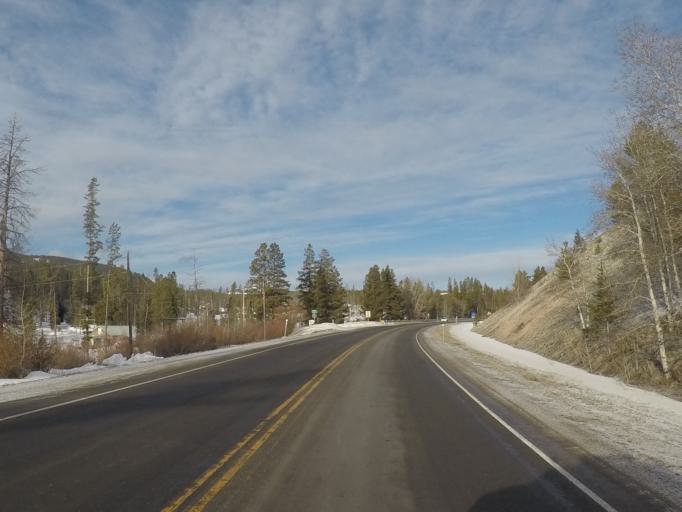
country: US
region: Montana
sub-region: Deer Lodge County
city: Anaconda
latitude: 46.1601
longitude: -113.1367
